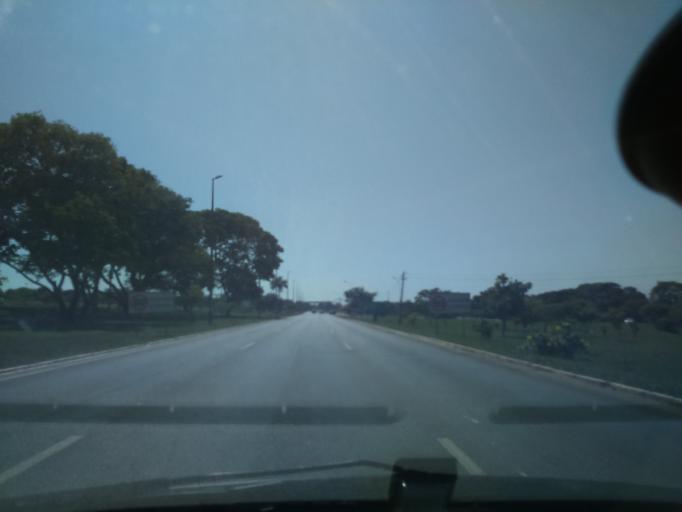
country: BR
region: Federal District
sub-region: Brasilia
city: Brasilia
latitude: -15.8202
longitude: -47.8812
